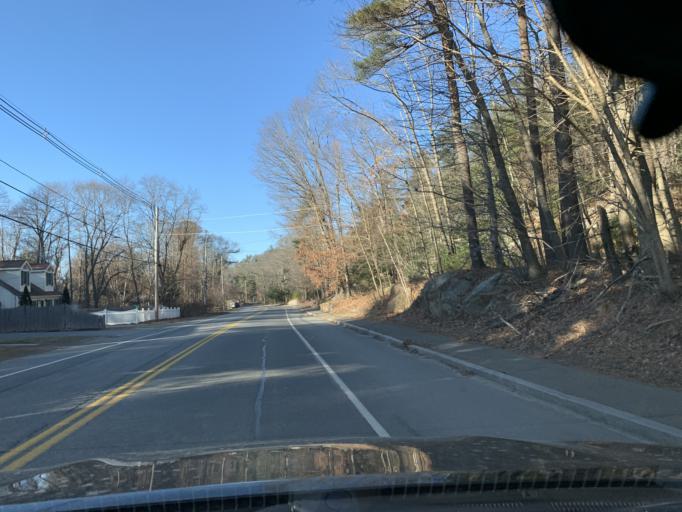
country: US
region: Massachusetts
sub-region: Essex County
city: Essex
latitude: 42.5864
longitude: -70.7824
